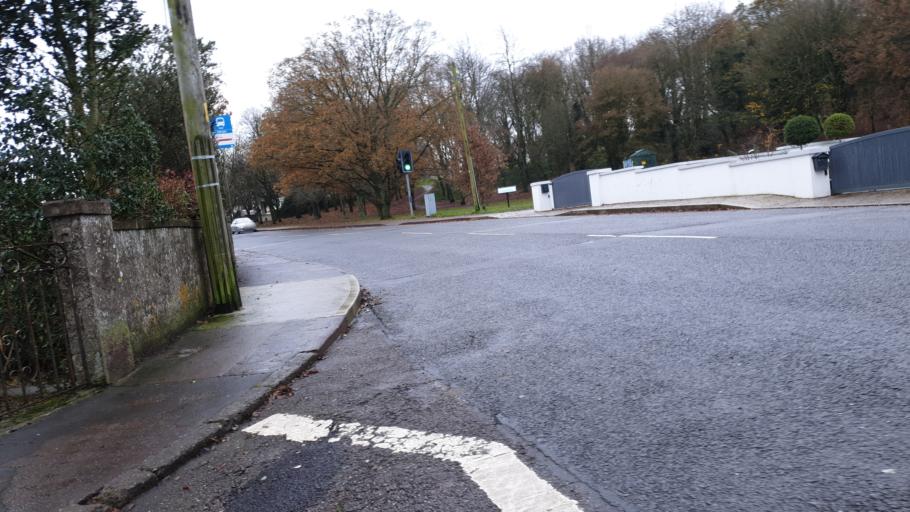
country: IE
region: Munster
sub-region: County Cork
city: Cork
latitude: 51.8927
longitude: -8.4294
